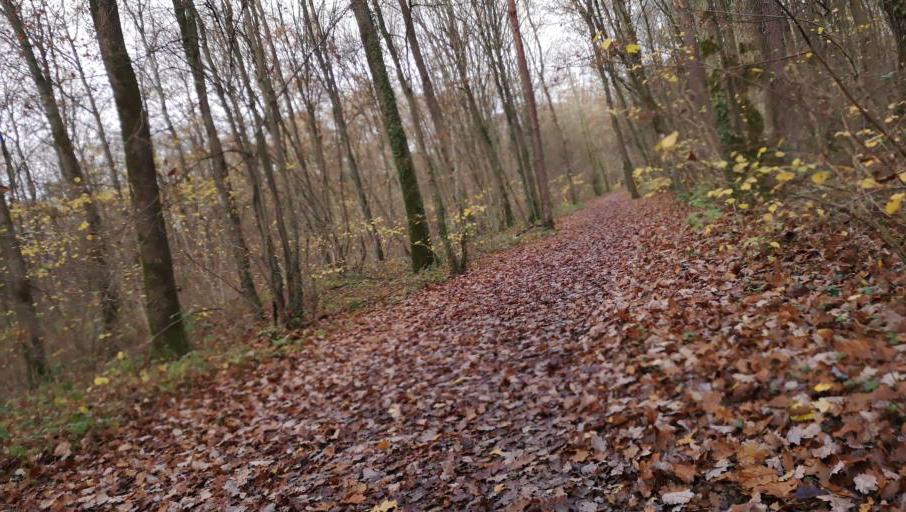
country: FR
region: Centre
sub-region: Departement du Loiret
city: Semoy
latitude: 47.9447
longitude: 1.9543
